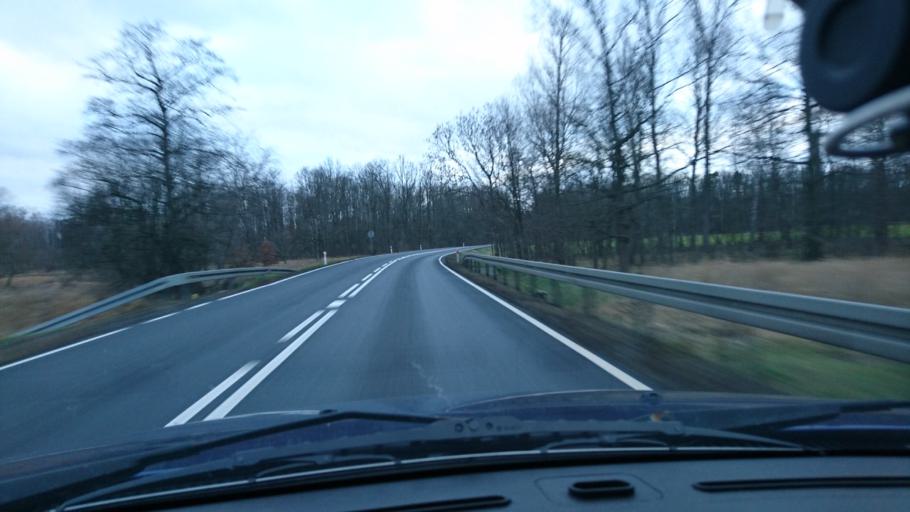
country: PL
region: Opole Voivodeship
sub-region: Powiat kluczborski
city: Byczyna
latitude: 51.1434
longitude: 18.1926
